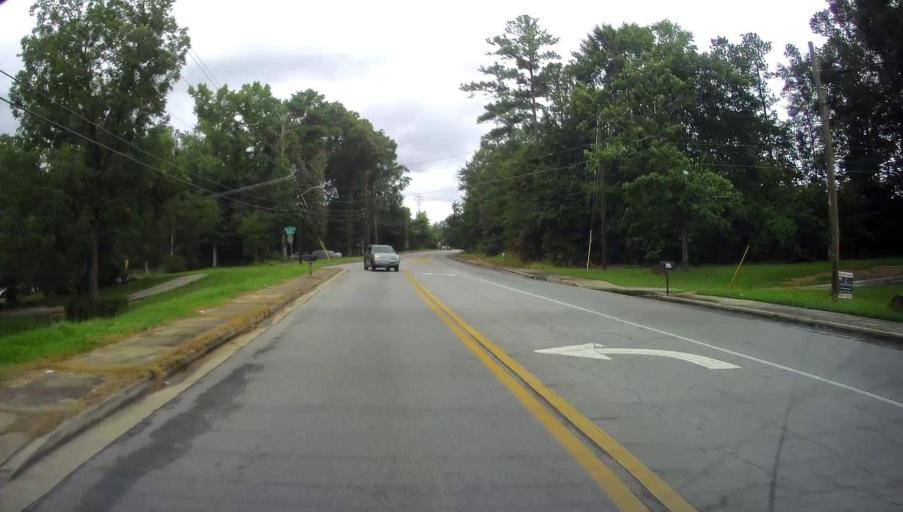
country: US
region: Georgia
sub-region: Bibb County
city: Macon
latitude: 32.7976
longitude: -83.6990
